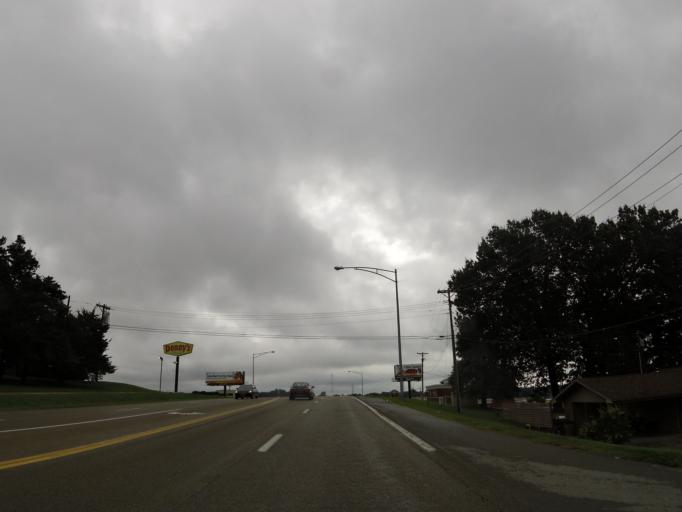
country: US
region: Missouri
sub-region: Cape Girardeau County
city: Cape Girardeau
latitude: 37.3034
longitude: -89.5603
